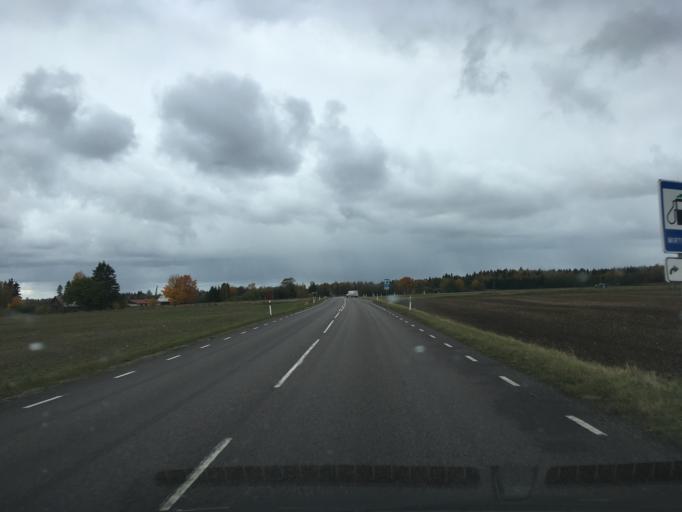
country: EE
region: Harju
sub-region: Anija vald
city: Kehra
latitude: 59.3283
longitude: 25.3234
